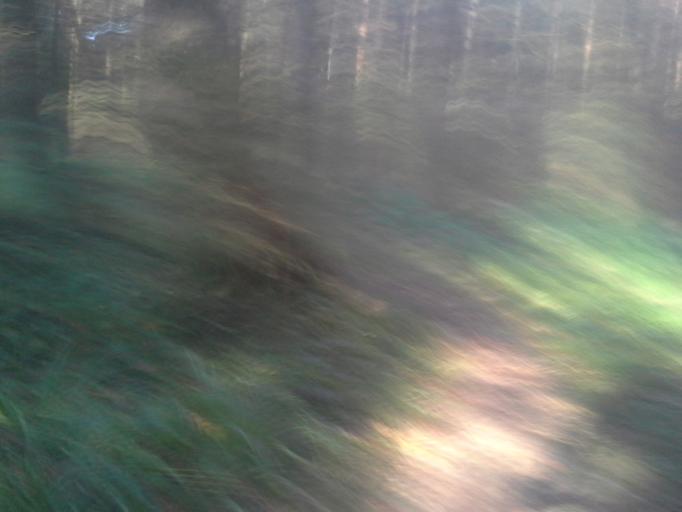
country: RU
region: Moskovskaya
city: Kievskij
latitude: 55.3591
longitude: 36.8990
